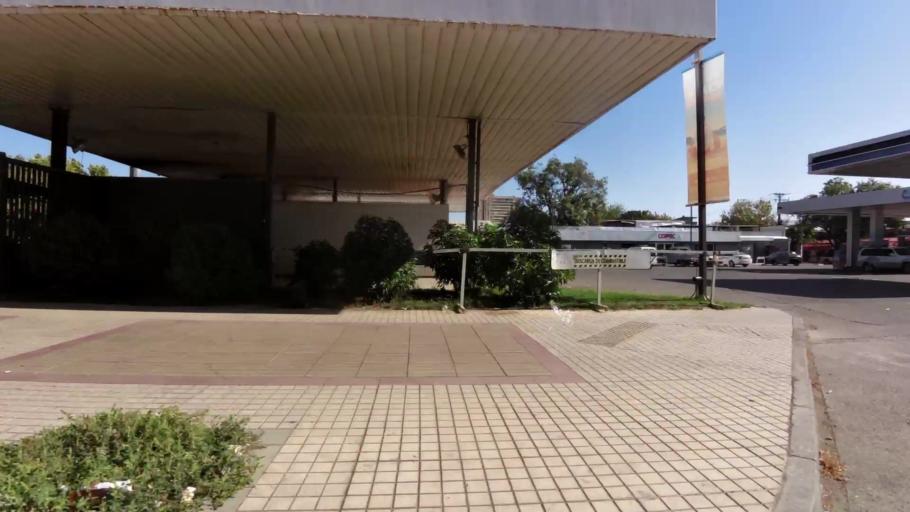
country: CL
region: Maule
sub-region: Provincia de Talca
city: Talca
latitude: -35.4253
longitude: -71.6577
